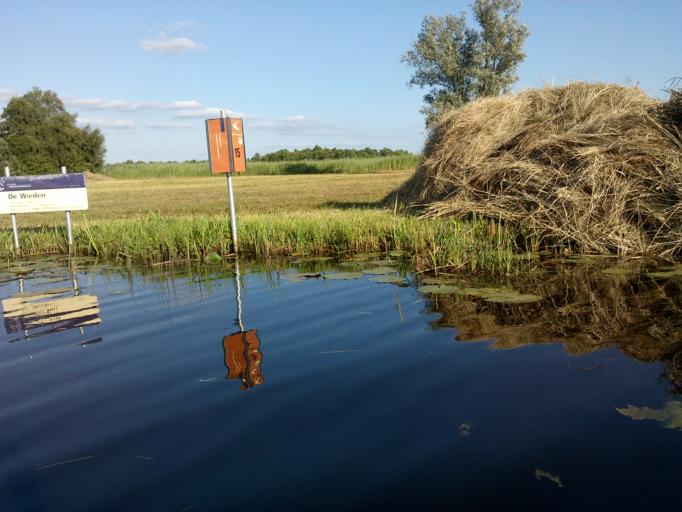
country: NL
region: Overijssel
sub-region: Gemeente Steenwijkerland
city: Sint Jansklooster
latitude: 52.6637
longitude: 6.0554
